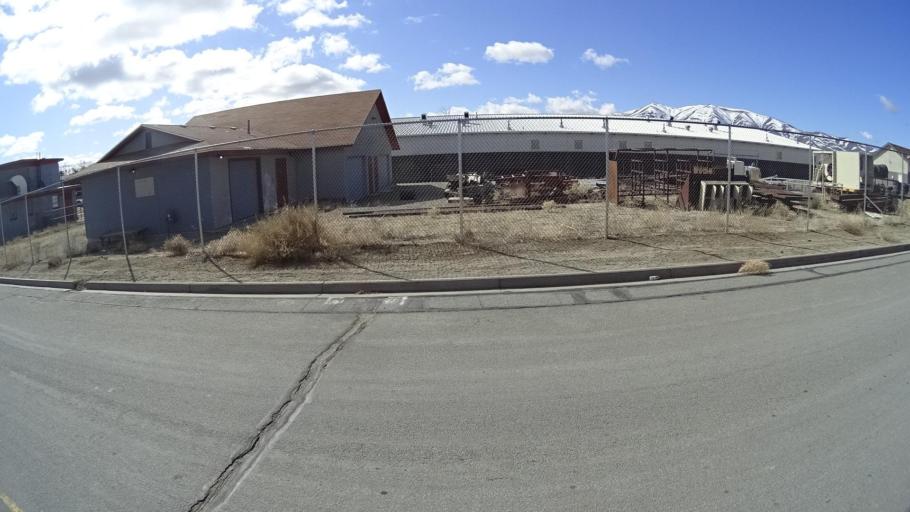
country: US
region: Nevada
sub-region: Washoe County
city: Lemmon Valley
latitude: 39.6577
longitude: -119.8769
